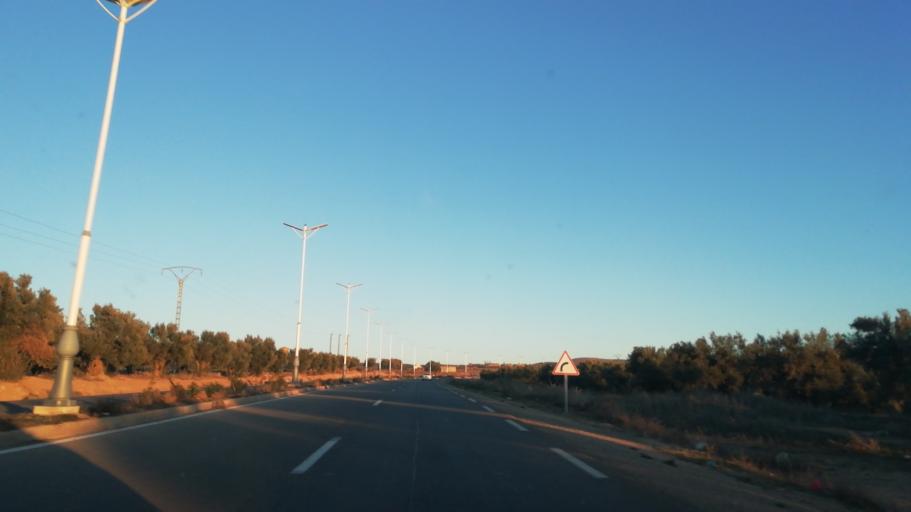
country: DZ
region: Saida
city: Saida
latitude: 34.8649
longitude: 0.1896
